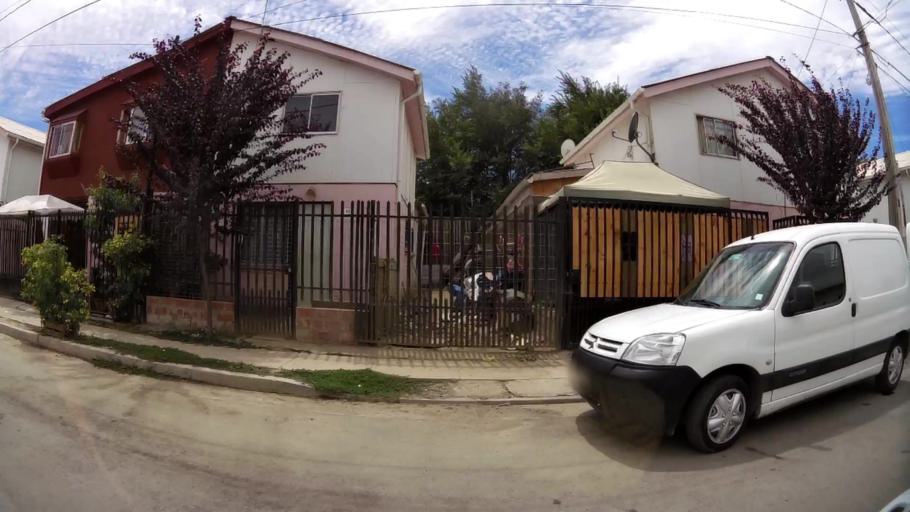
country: CL
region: O'Higgins
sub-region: Provincia de Cachapoal
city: Graneros
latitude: -34.0722
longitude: -70.7391
